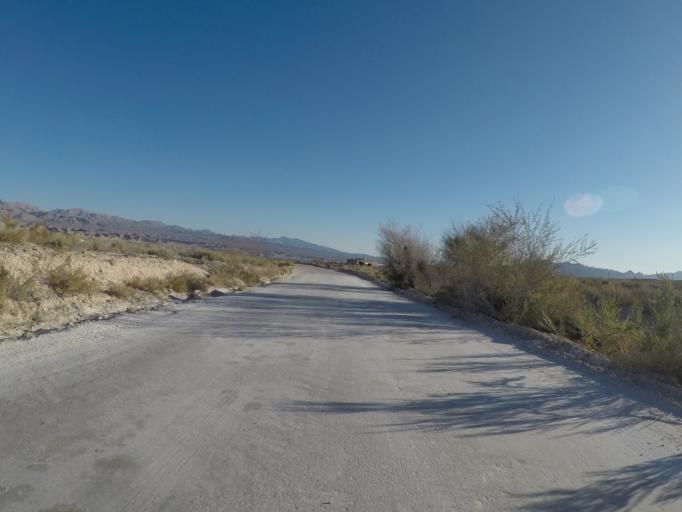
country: US
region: Nevada
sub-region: Clark County
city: Moapa Valley
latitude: 36.3826
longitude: -114.4086
